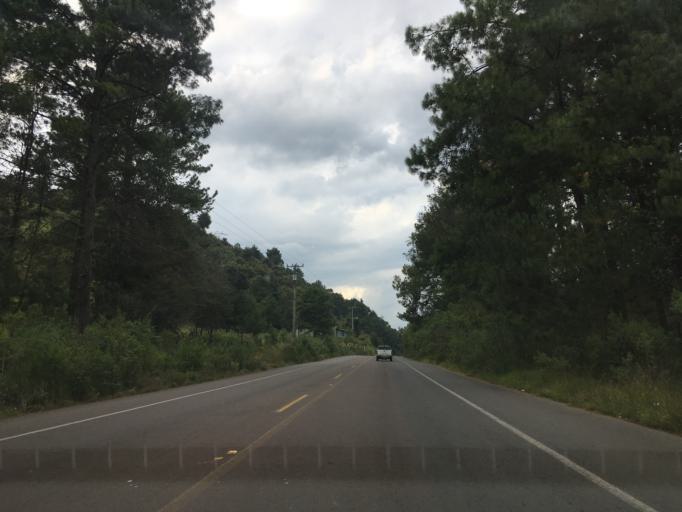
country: MX
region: Michoacan
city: Angahuan
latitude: 19.5266
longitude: -102.1889
